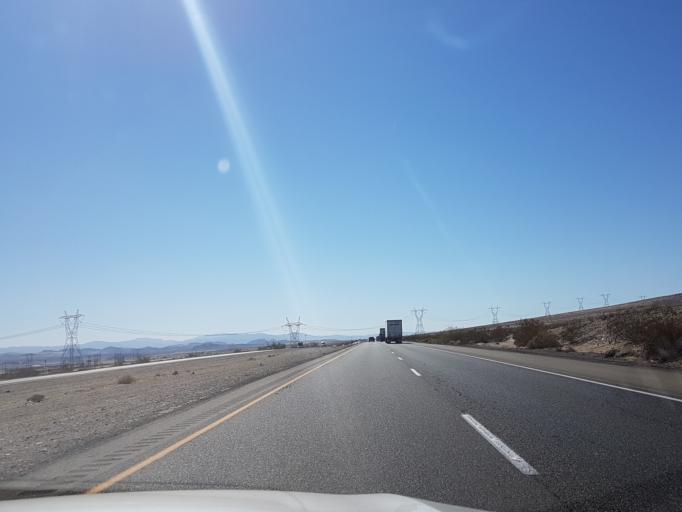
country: US
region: California
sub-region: San Bernardino County
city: Fort Irwin
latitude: 35.0559
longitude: -116.4357
